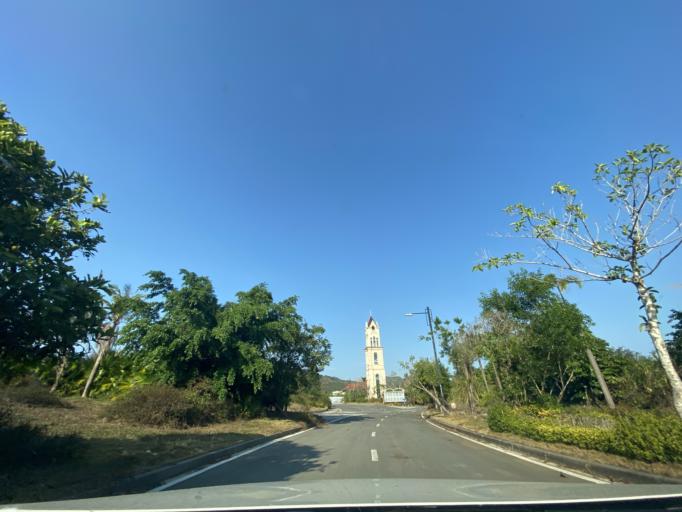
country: CN
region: Hainan
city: Yingzhou
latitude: 18.4524
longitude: 109.8548
